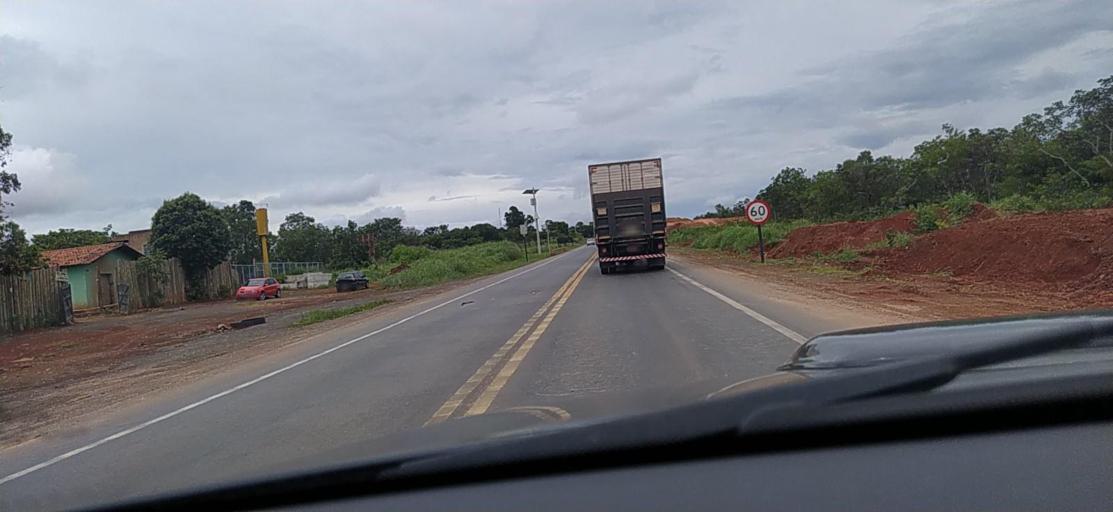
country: BR
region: Minas Gerais
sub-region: Curvelo
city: Curvelo
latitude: -18.7161
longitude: -44.4425
